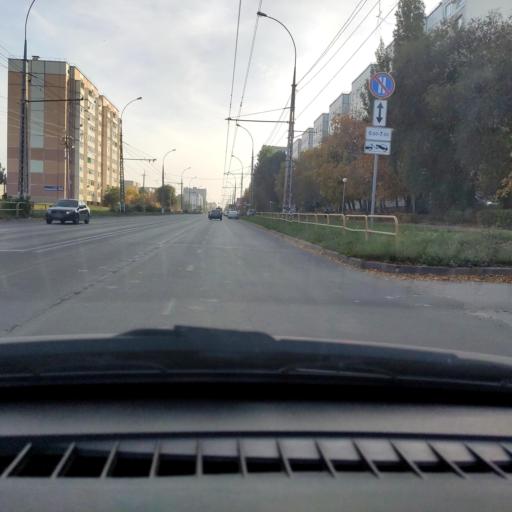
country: RU
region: Samara
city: Tol'yatti
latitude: 53.5357
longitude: 49.3044
